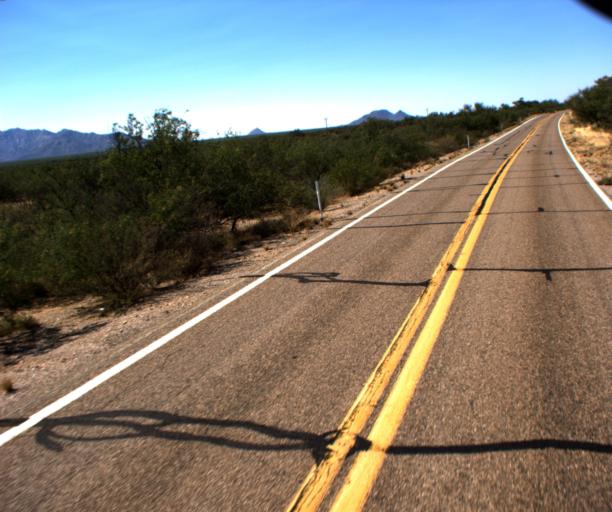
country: US
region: Arizona
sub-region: Pima County
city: Three Points
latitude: 31.9159
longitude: -111.3906
